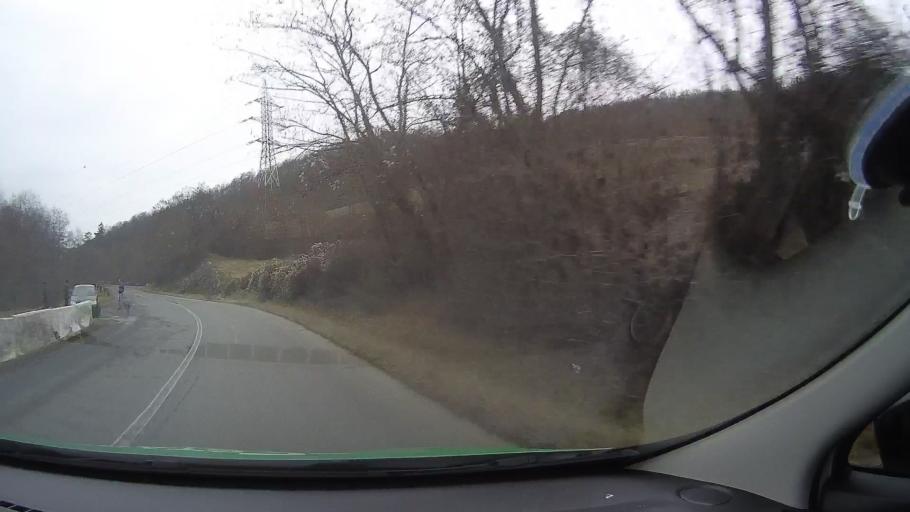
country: RO
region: Alba
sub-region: Comuna Ighiu
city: Ighiel
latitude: 46.1004
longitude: 23.4712
